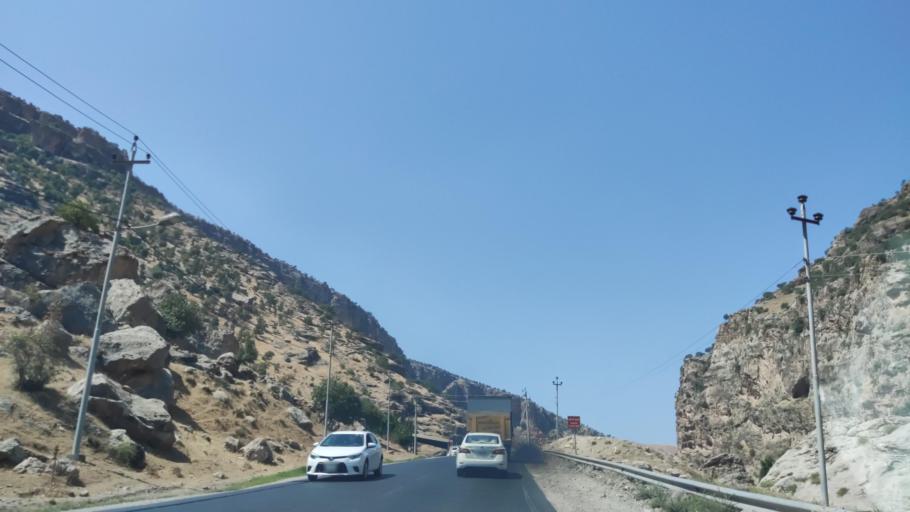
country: IQ
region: Arbil
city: Ruwandiz
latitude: 36.6297
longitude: 44.4414
